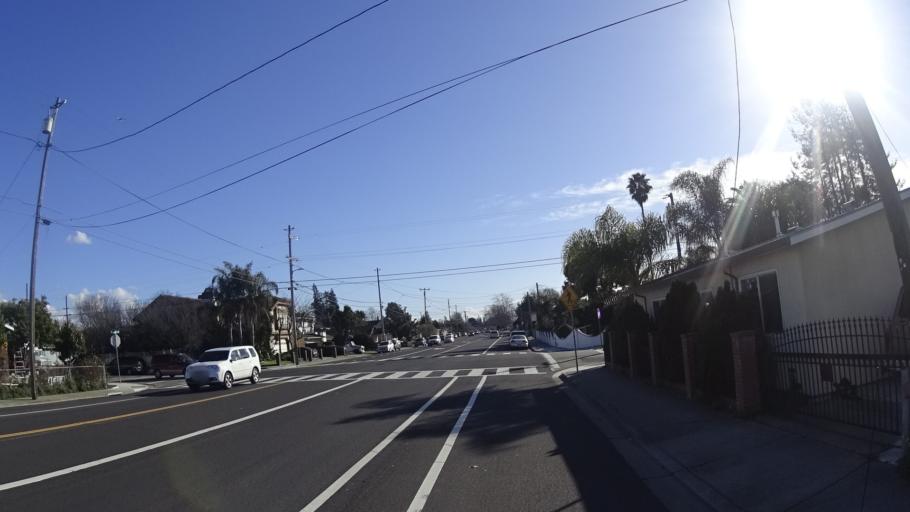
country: US
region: California
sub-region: Alameda County
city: Cherryland
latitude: 37.6652
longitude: -122.1023
